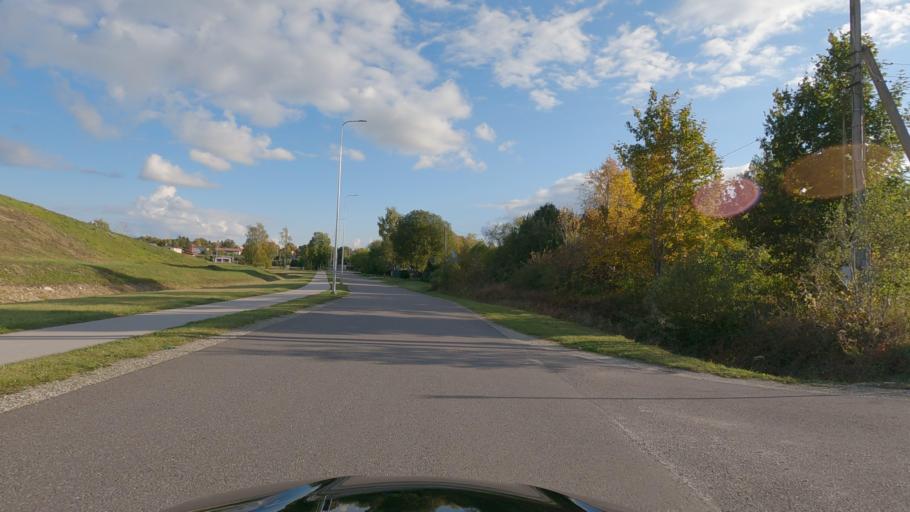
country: EE
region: Harju
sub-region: Saku vald
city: Saku
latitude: 59.3034
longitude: 24.6503
